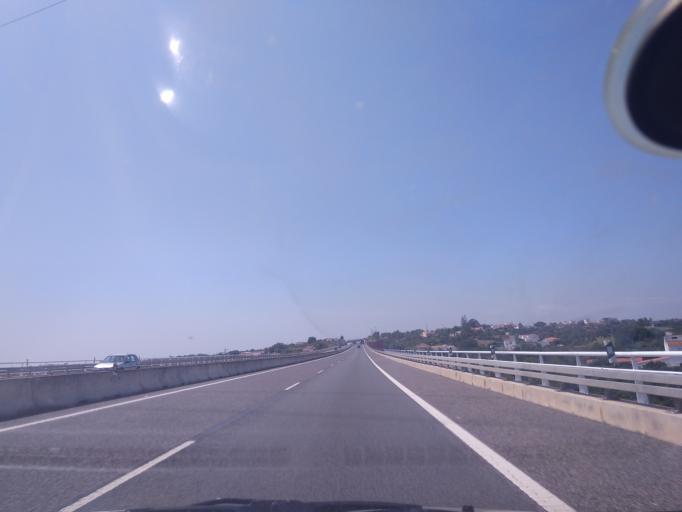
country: PT
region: Faro
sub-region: Lagoa
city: Lagoa
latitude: 37.1432
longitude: -8.4168
